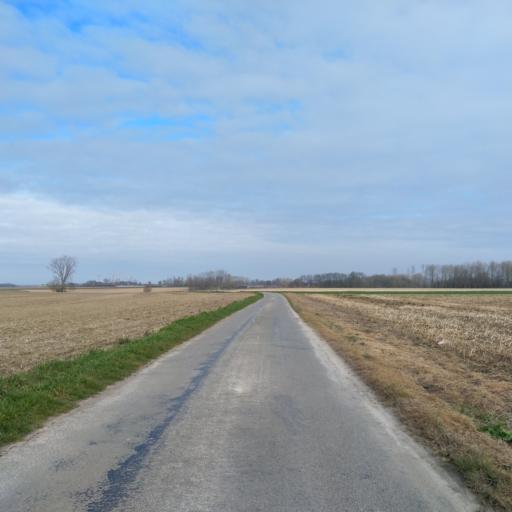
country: BE
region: Wallonia
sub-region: Province du Hainaut
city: Lens
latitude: 50.5722
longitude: 3.8986
